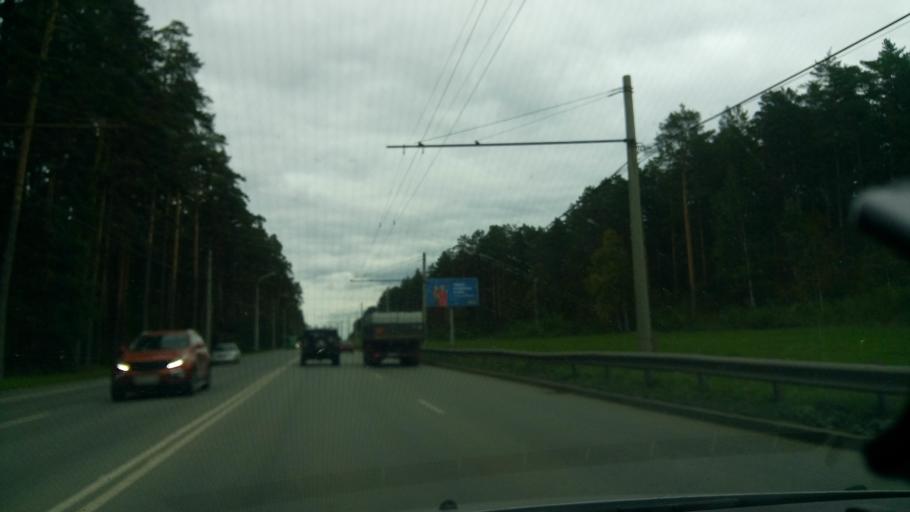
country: RU
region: Sverdlovsk
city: Sovkhoznyy
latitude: 56.7828
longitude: 60.5620
